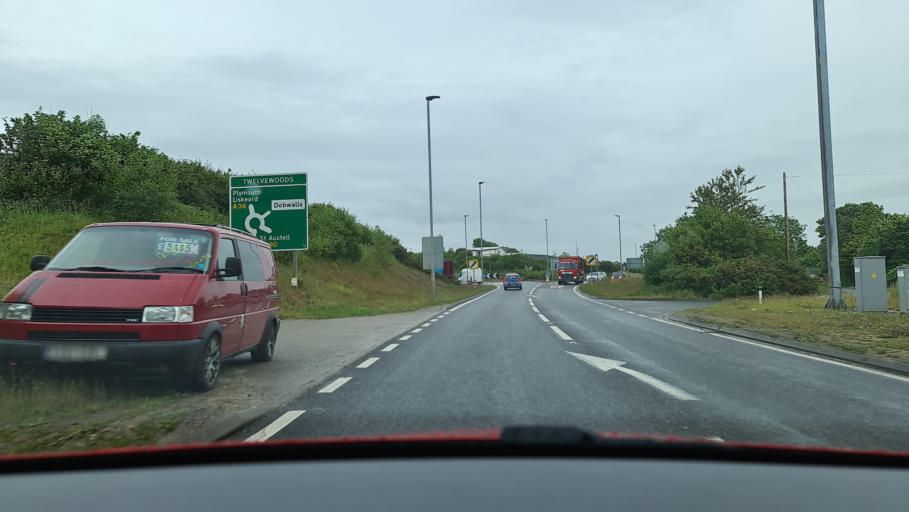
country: GB
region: England
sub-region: Cornwall
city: Liskeard
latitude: 50.4586
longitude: -4.5284
